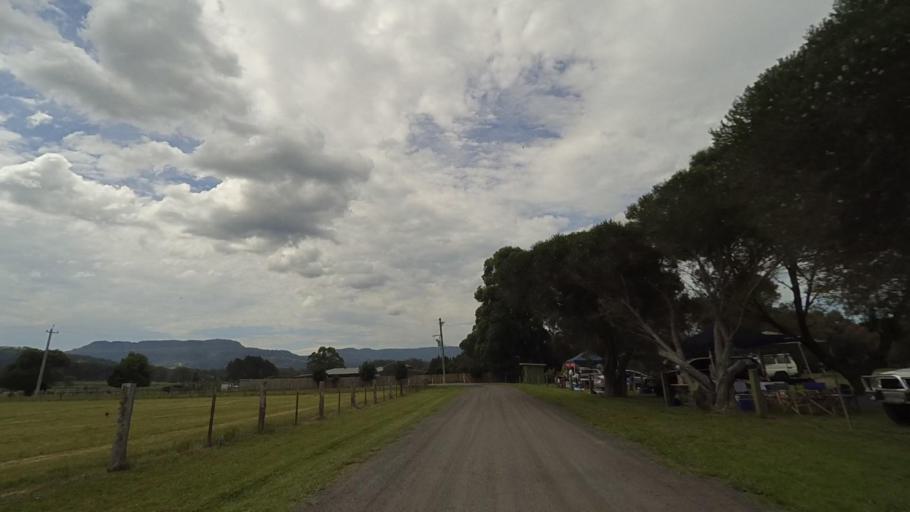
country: AU
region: New South Wales
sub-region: Shoalhaven Shire
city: Berry
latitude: -34.7932
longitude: 150.6744
